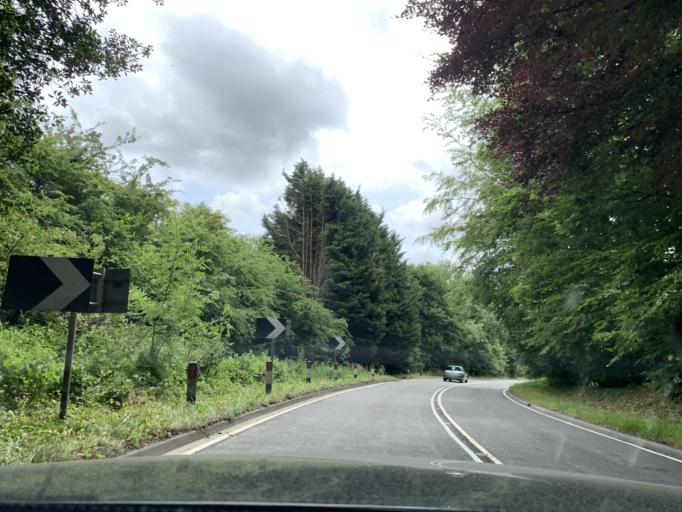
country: GB
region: England
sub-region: East Sussex
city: Robertsbridge
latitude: 51.0013
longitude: 0.4773
